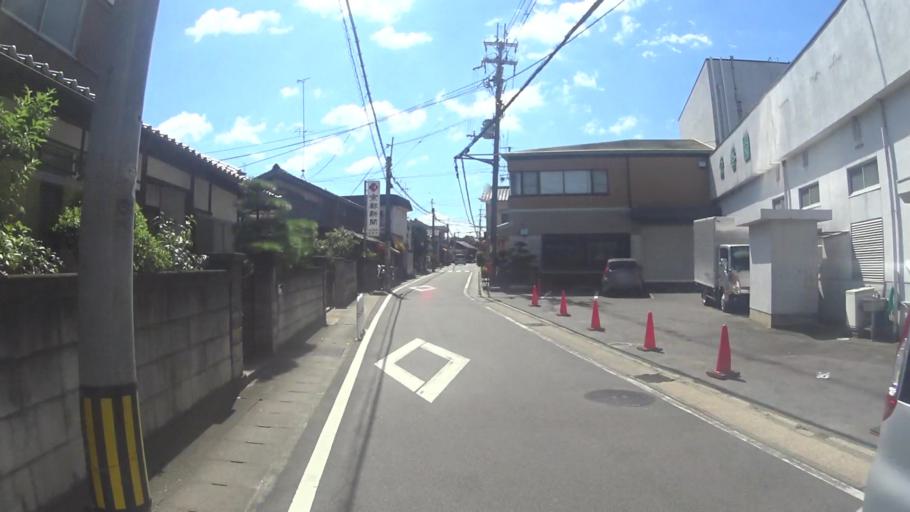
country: JP
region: Kyoto
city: Tanabe
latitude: 34.8206
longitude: 135.8070
